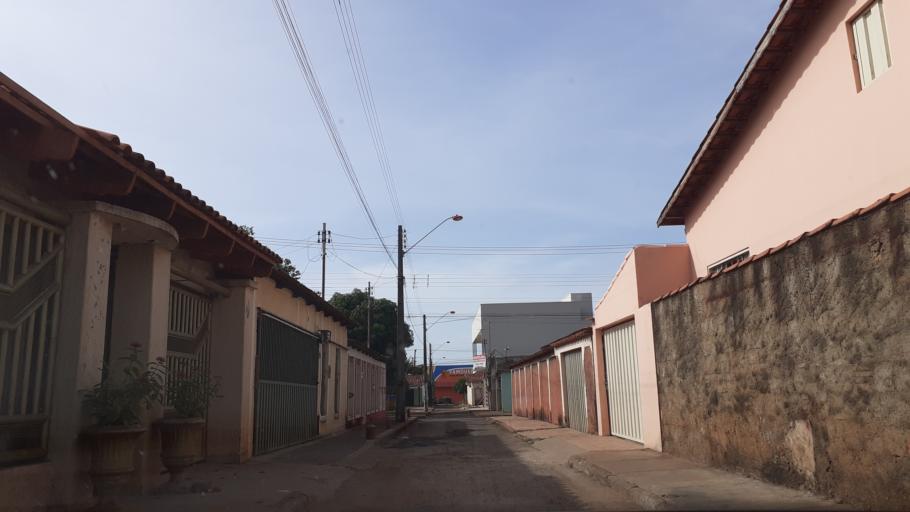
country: BR
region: Goias
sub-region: Itumbiara
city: Itumbiara
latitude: -18.4153
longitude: -49.2377
